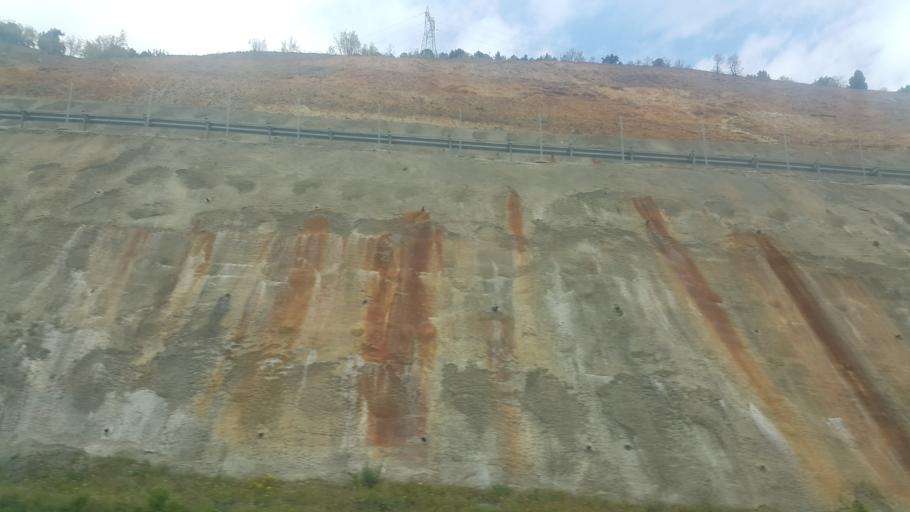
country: TR
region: Nigde
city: Ciftehan
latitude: 37.5392
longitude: 34.7928
